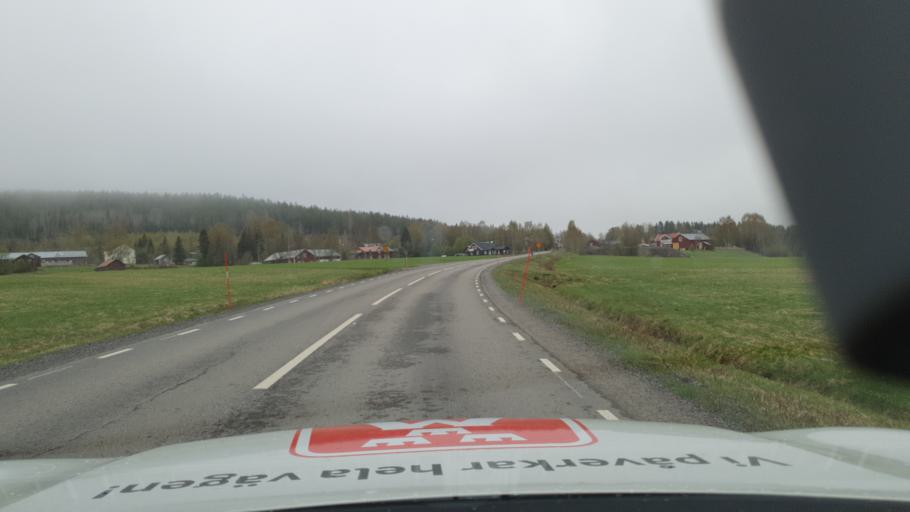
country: SE
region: Vaesterbotten
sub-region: Vannas Kommun
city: Vannasby
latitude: 63.7785
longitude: 19.8471
